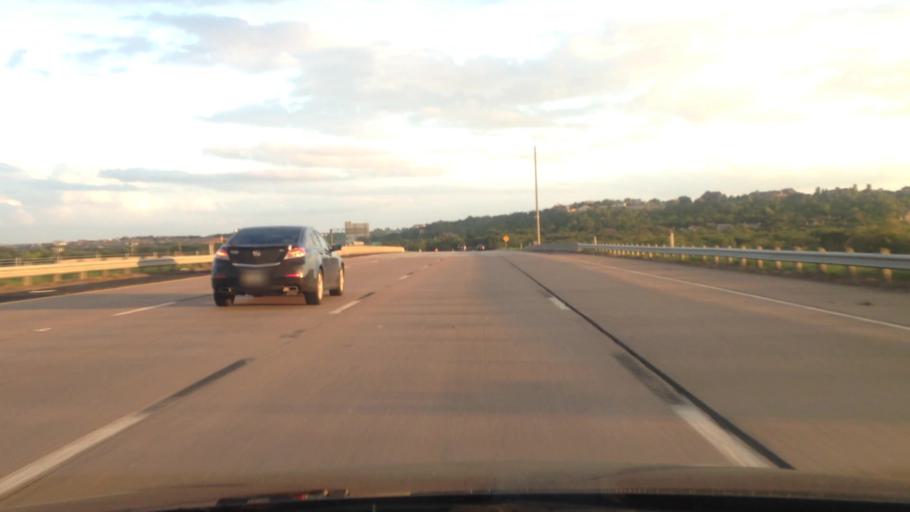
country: US
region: Texas
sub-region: Tarrant County
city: White Settlement
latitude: 32.7193
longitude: -97.4796
